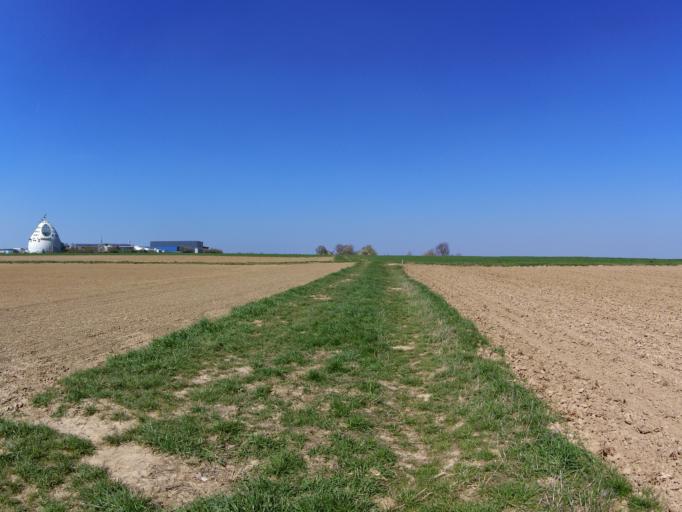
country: DE
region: Bavaria
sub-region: Regierungsbezirk Unterfranken
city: Biebelried
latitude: 49.7761
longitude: 10.0759
